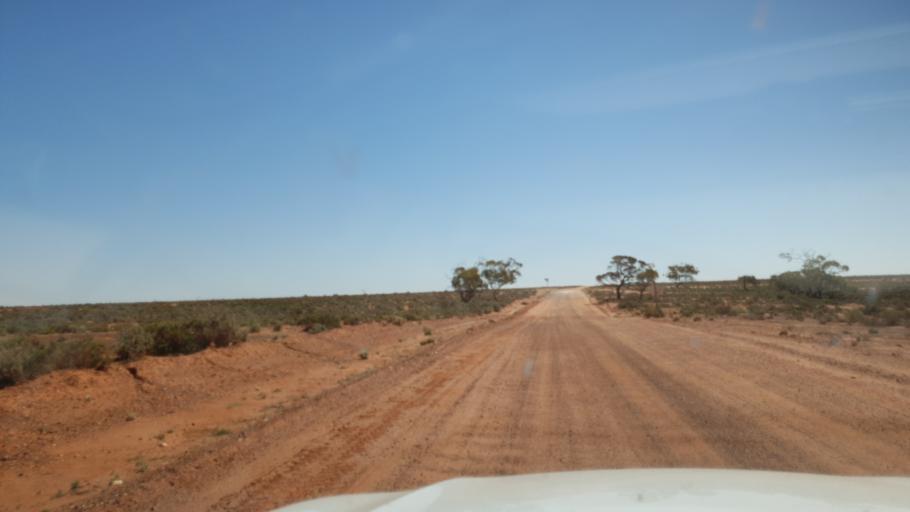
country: AU
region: South Australia
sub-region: Whyalla
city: Whyalla
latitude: -32.6471
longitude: 136.9597
